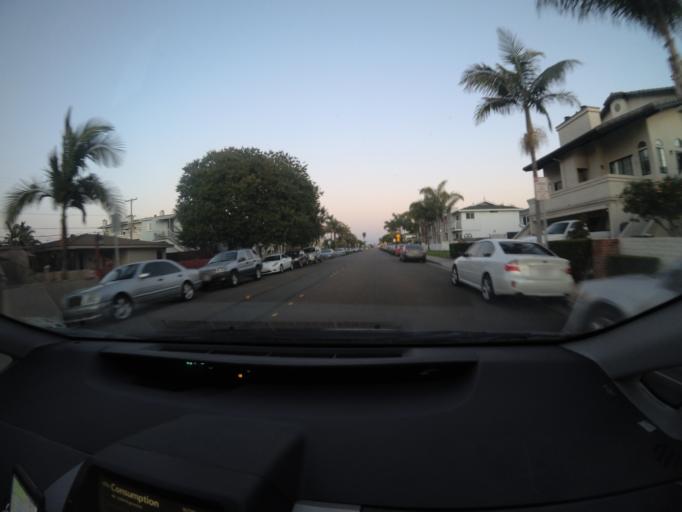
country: US
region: California
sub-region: San Diego County
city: Imperial Beach
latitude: 32.5803
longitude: -117.1294
